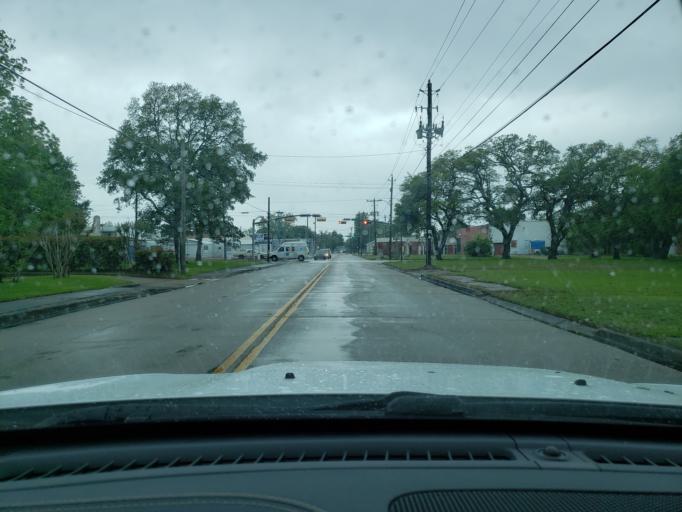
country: US
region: Texas
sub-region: Harris County
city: Baytown
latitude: 29.7350
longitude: -94.9722
